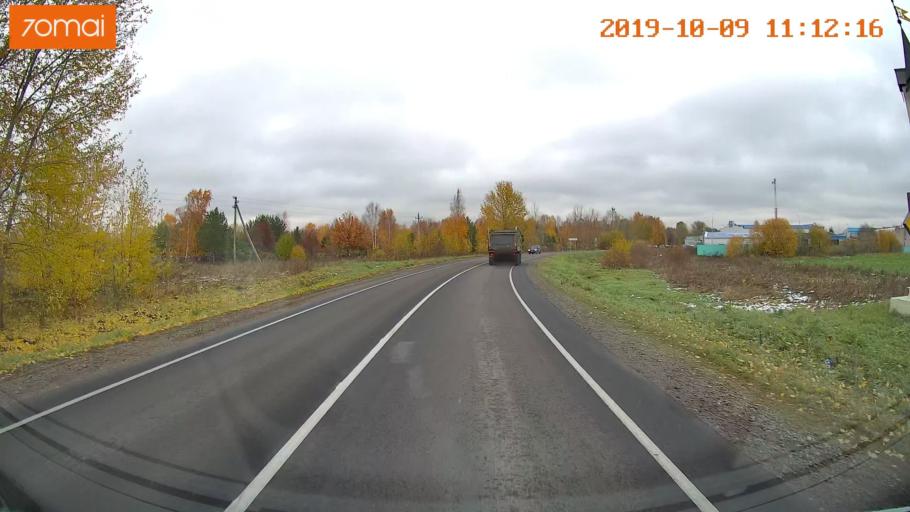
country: RU
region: Vologda
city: Vologda
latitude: 59.1761
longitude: 39.8284
